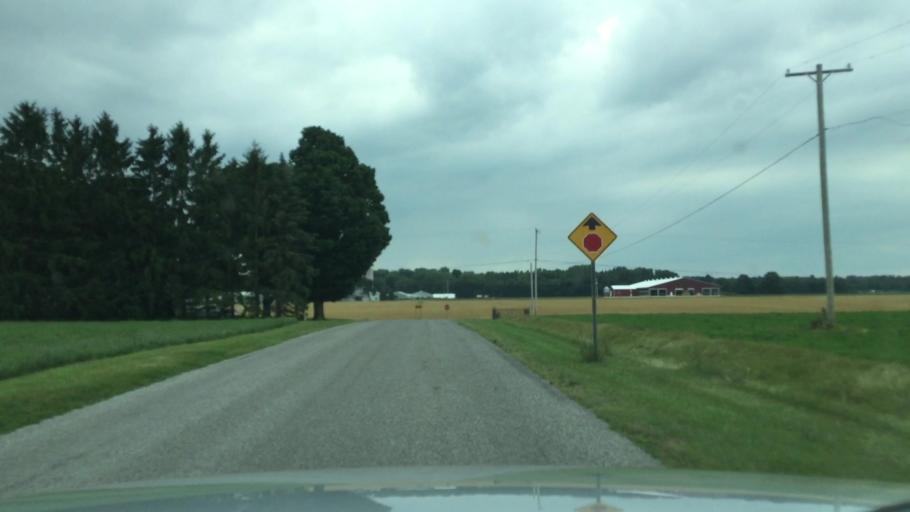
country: US
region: Michigan
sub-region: Saginaw County
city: Birch Run
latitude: 43.3084
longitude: -83.7956
